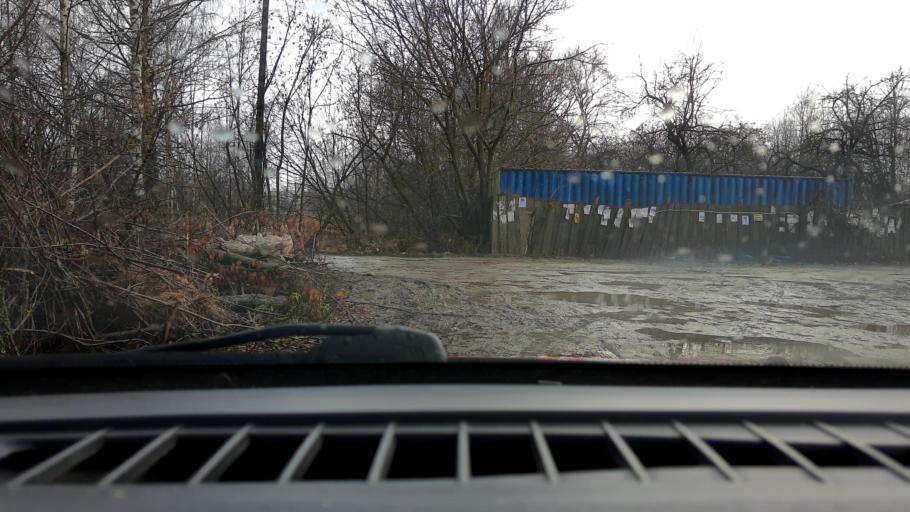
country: RU
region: Nizjnij Novgorod
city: Gorbatovka
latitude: 56.3130
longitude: 43.8391
